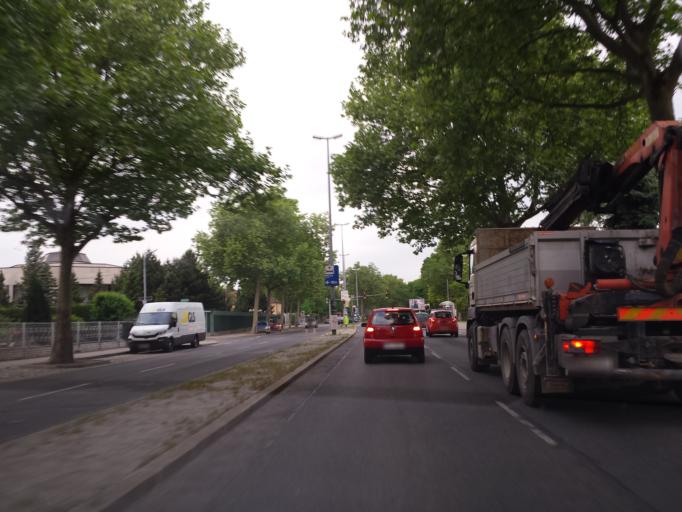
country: AT
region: Lower Austria
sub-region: Politischer Bezirk Wien-Umgebung
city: Gerasdorf bei Wien
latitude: 48.2236
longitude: 16.4708
